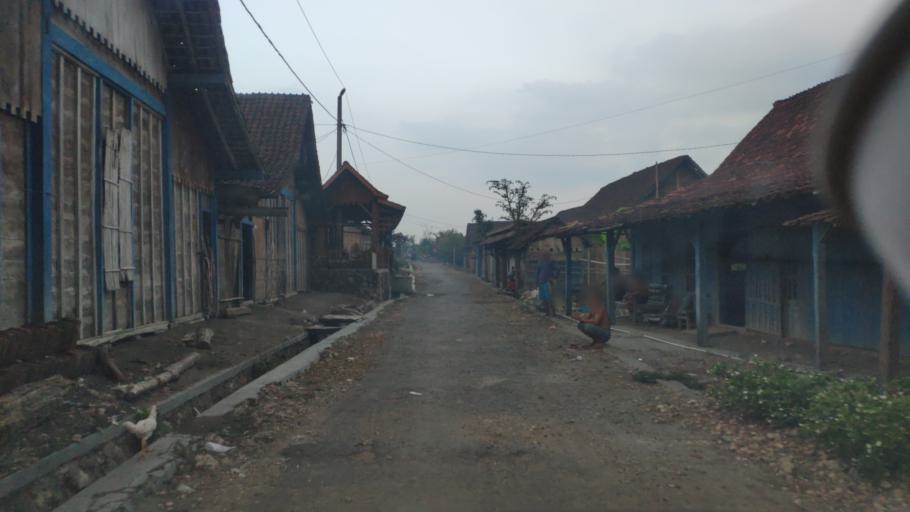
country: ID
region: Central Java
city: Temanjang
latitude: -7.1134
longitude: 111.3933
